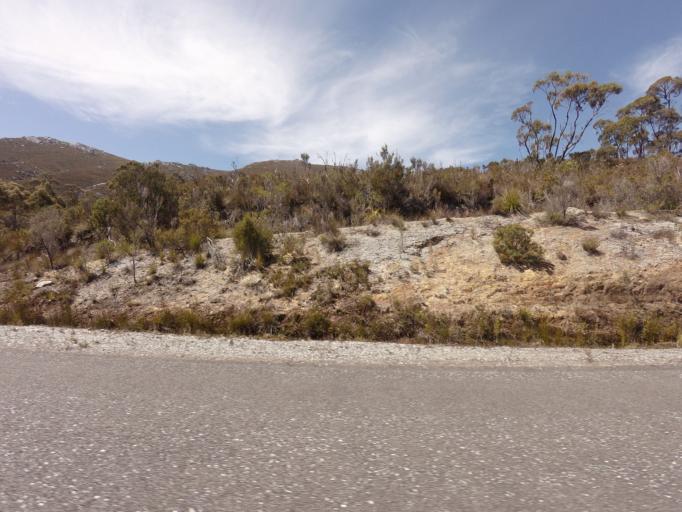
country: AU
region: Tasmania
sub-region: West Coast
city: Queenstown
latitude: -42.7778
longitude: 146.0573
